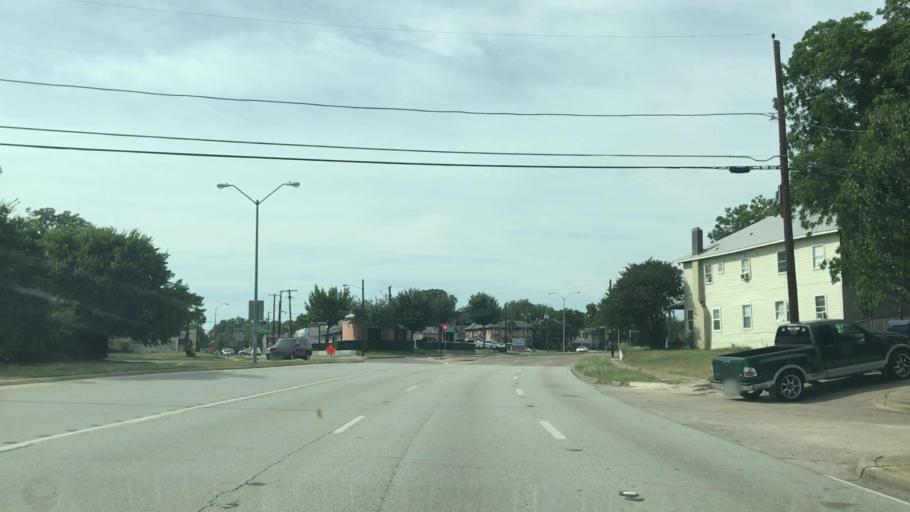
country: US
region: Texas
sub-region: Dallas County
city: Dallas
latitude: 32.7952
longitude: -96.7605
